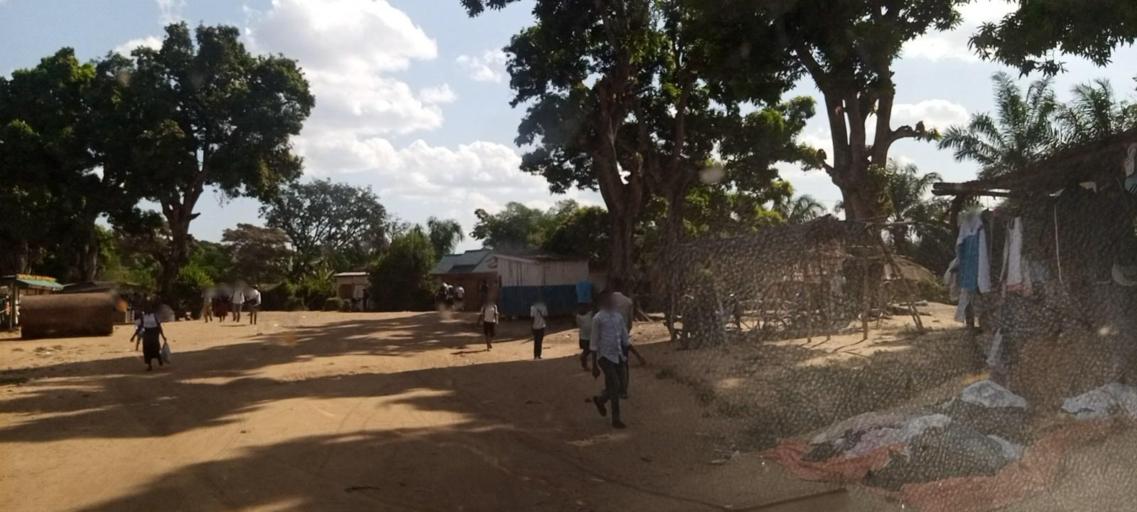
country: CD
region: Kasai-Oriental
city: Kabinda
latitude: -6.1312
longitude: 24.4900
